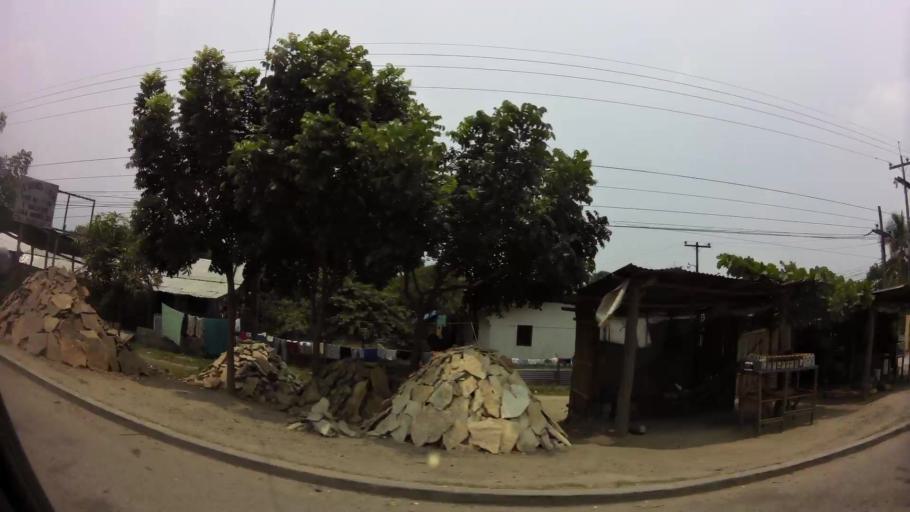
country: HN
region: Yoro
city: El Progreso
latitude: 15.4050
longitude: -87.8234
